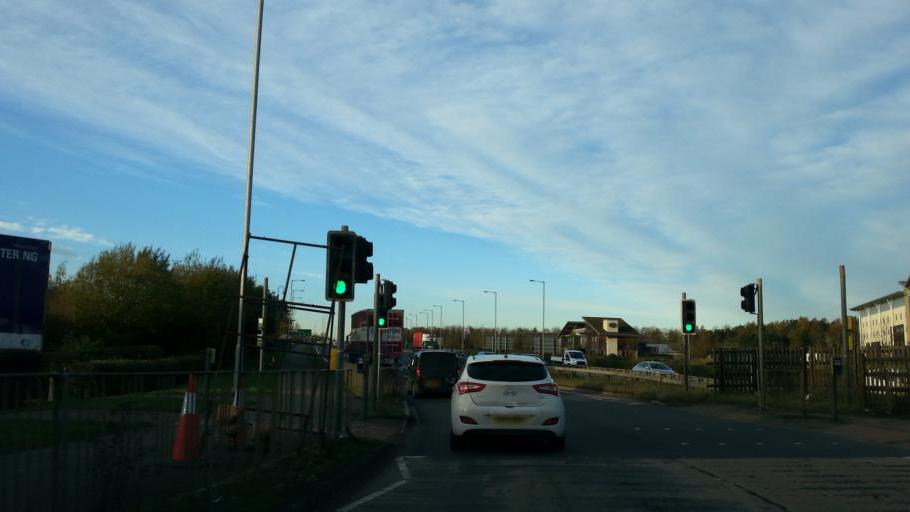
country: GB
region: England
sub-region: Northamptonshire
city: Kettering
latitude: 52.4215
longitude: -0.7283
